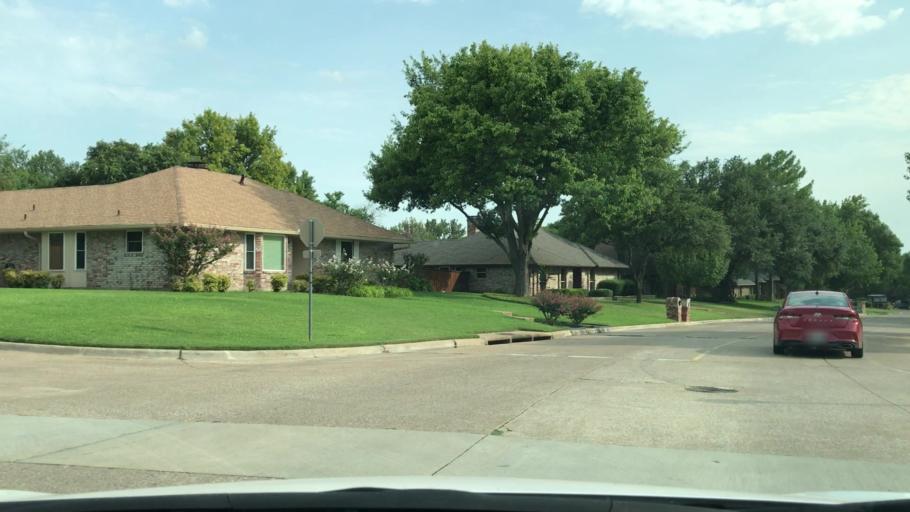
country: US
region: Texas
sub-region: Rockwall County
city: Rockwall
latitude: 32.9277
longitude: -96.4686
